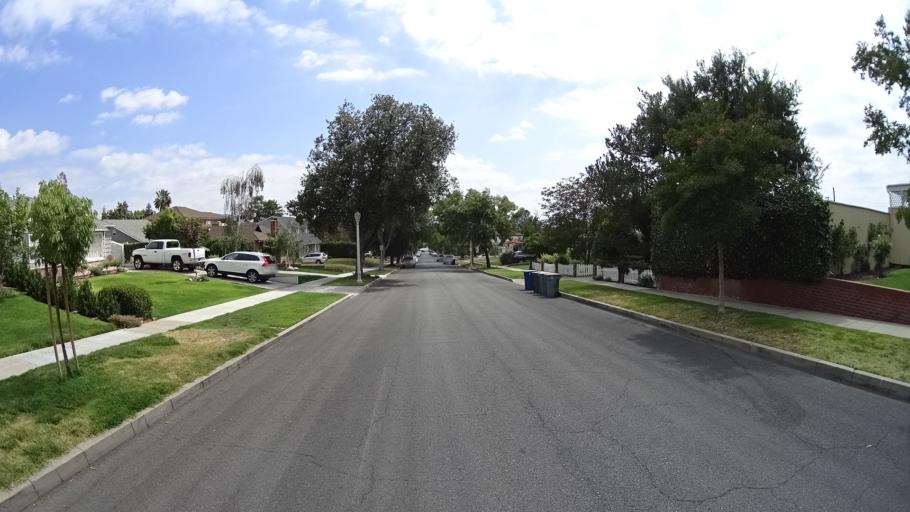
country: US
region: California
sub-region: Los Angeles County
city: Burbank
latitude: 34.1931
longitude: -118.3146
